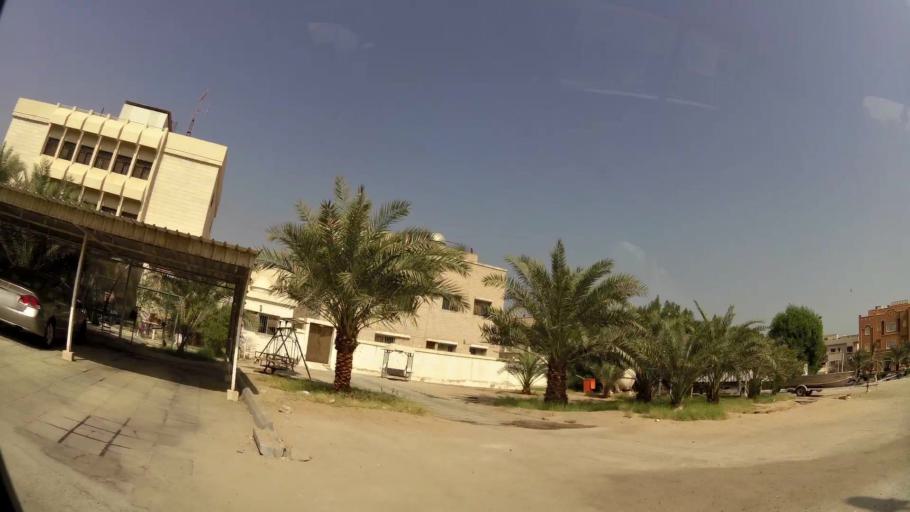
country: KW
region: Al Asimah
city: Ad Dasmah
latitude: 29.3549
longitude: 48.0102
